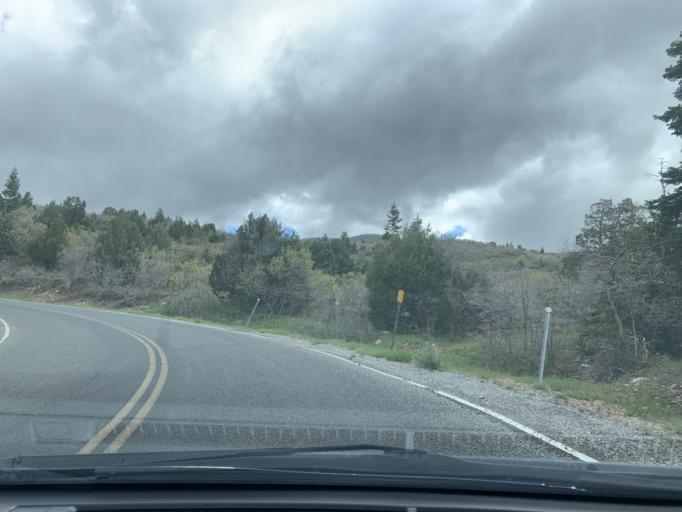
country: US
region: Utah
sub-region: Sanpete County
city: Fountain Green
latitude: 39.7801
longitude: -111.6906
